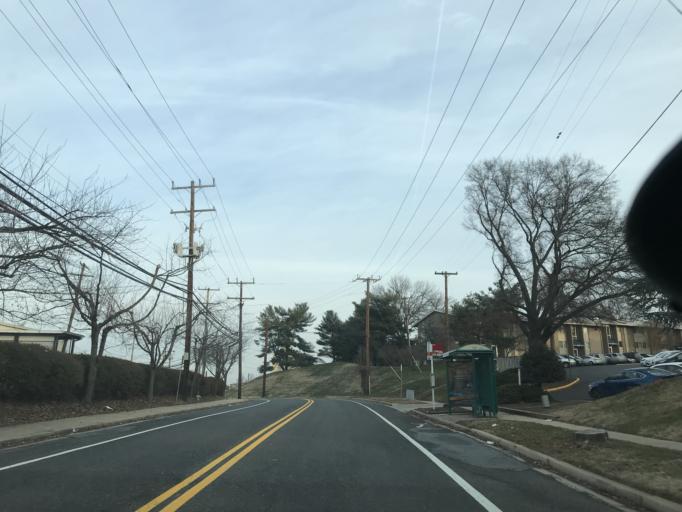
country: US
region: Maryland
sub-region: Prince George's County
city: Lanham
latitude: 38.9558
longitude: -76.8683
